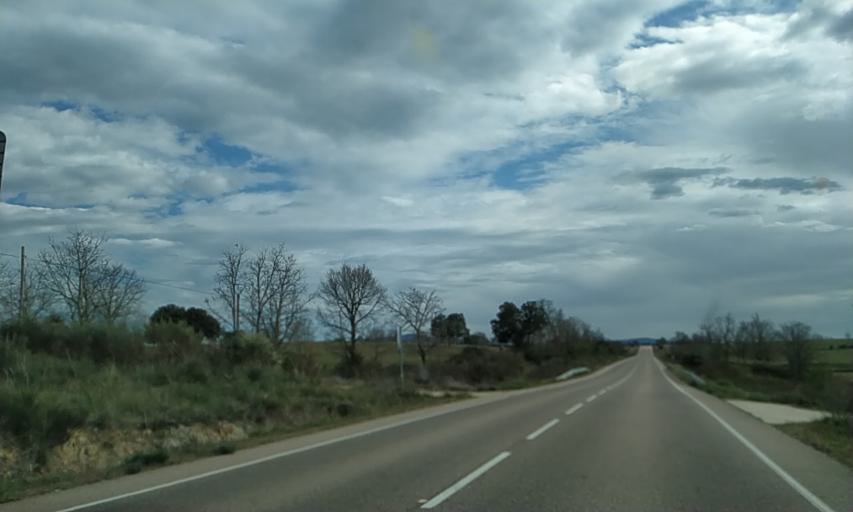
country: ES
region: Castille and Leon
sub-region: Provincia de Salamanca
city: Robleda
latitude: 40.4163
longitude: -6.6017
